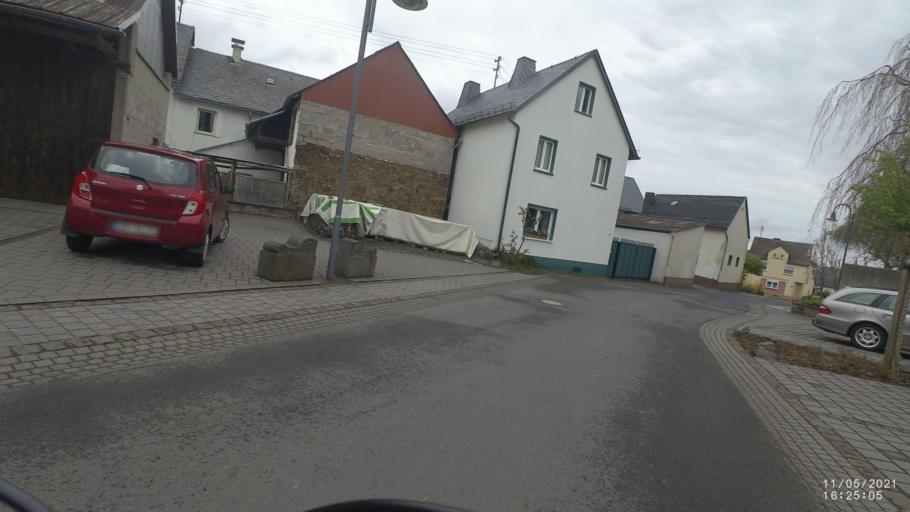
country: DE
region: Rheinland-Pfalz
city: Nachtsheim
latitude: 50.3175
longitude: 7.0622
